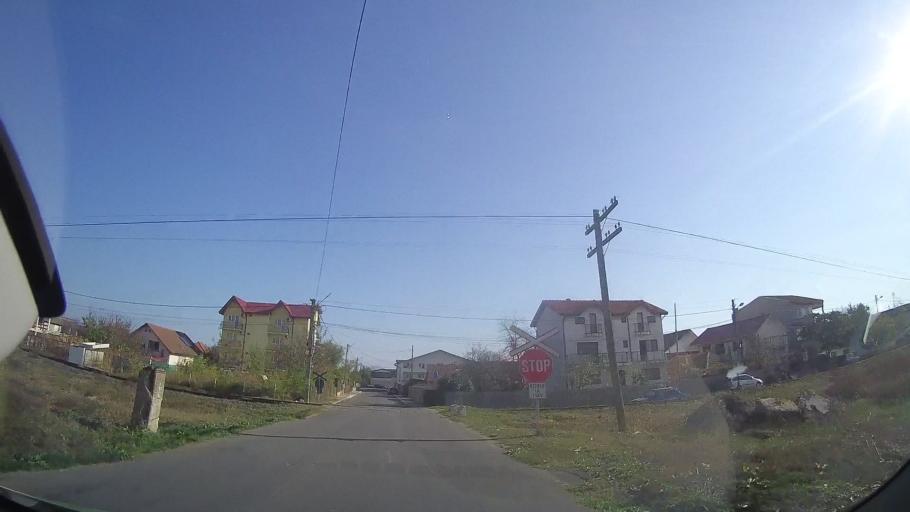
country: RO
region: Constanta
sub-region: Comuna Costinesti
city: Costinesti
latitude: 43.9537
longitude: 28.6325
